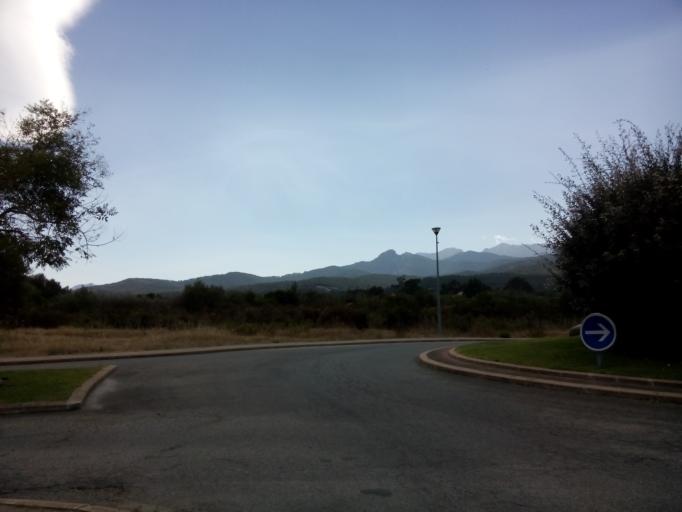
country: FR
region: Corsica
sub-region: Departement de la Haute-Corse
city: Ventiseri
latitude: 41.9180
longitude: 9.3875
